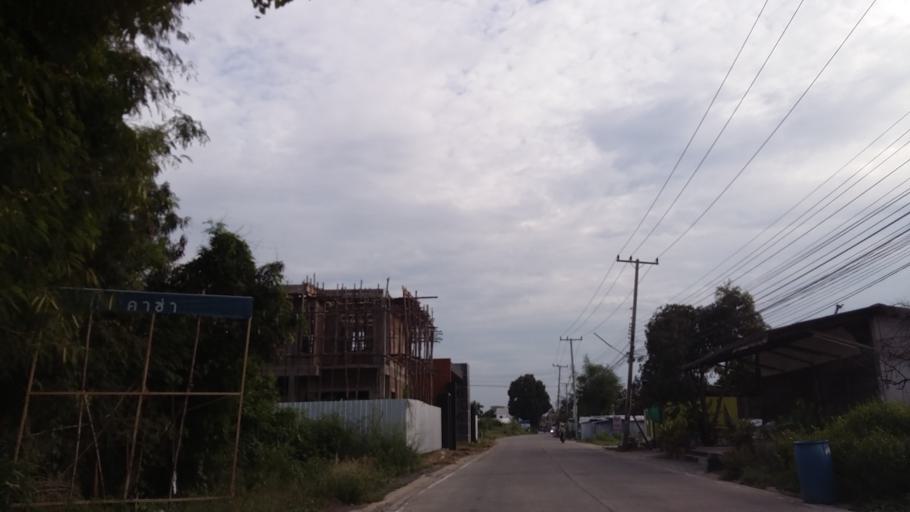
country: TH
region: Chon Buri
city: Chon Buri
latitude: 13.3132
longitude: 100.9379
